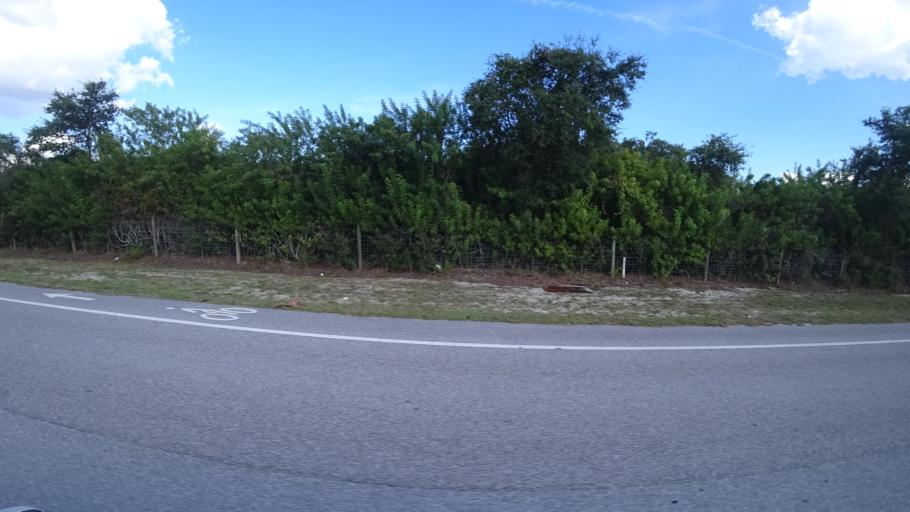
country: US
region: Florida
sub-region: Manatee County
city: West Bradenton
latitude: 27.4582
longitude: -82.6368
